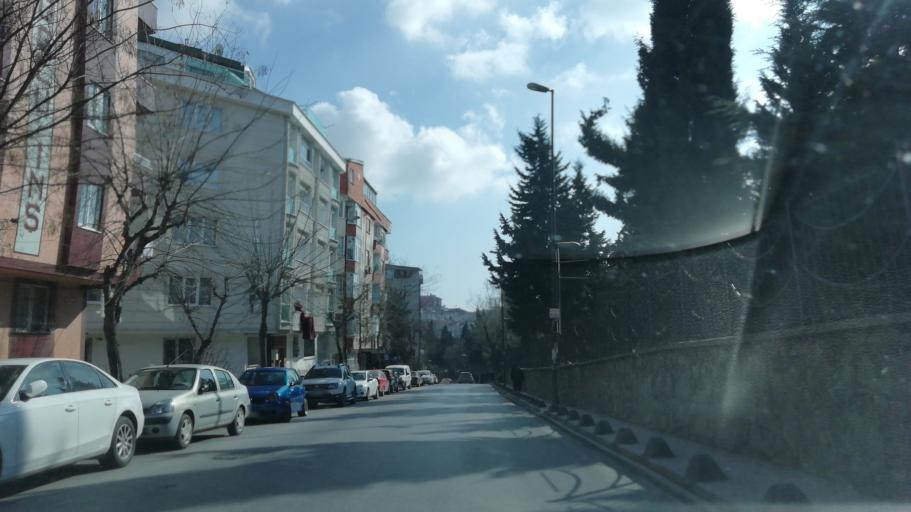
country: TR
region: Istanbul
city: Bahcelievler
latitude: 41.0164
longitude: 28.8372
